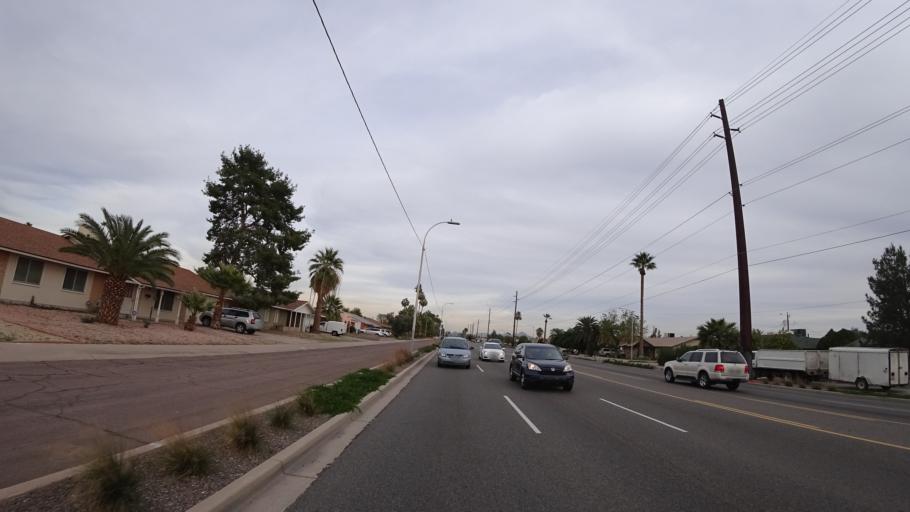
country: US
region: Arizona
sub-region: Maricopa County
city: Glendale
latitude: 33.5676
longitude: -112.1481
